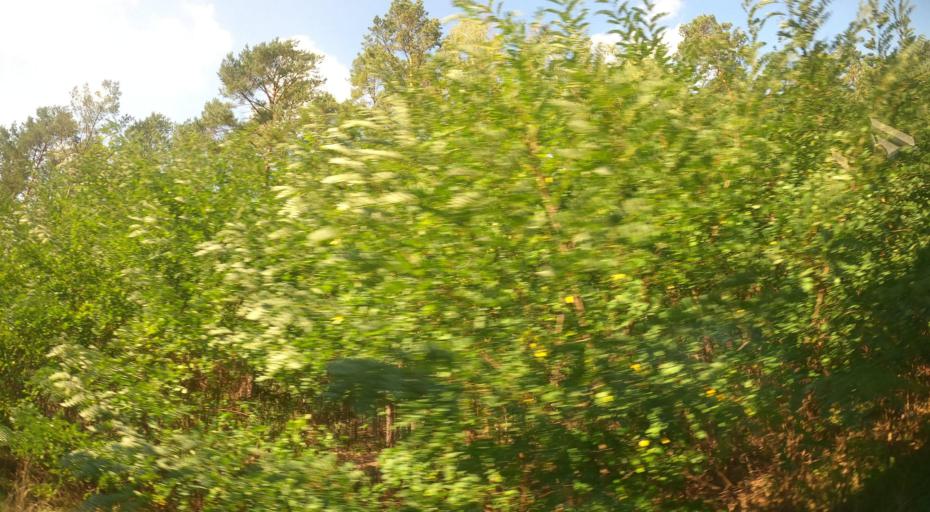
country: PL
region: Lubusz
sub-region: Powiat zielonogorski
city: Swidnica
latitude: 51.9268
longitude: 15.3838
